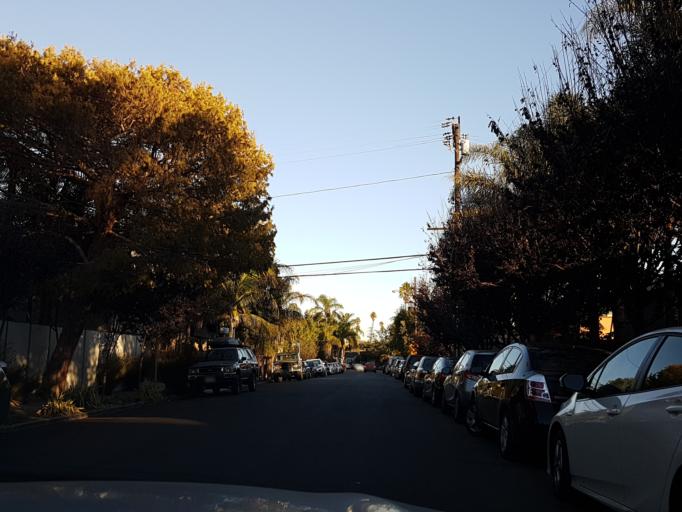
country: US
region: California
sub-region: Los Angeles County
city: Marina del Rey
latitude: 33.9921
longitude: -118.4624
